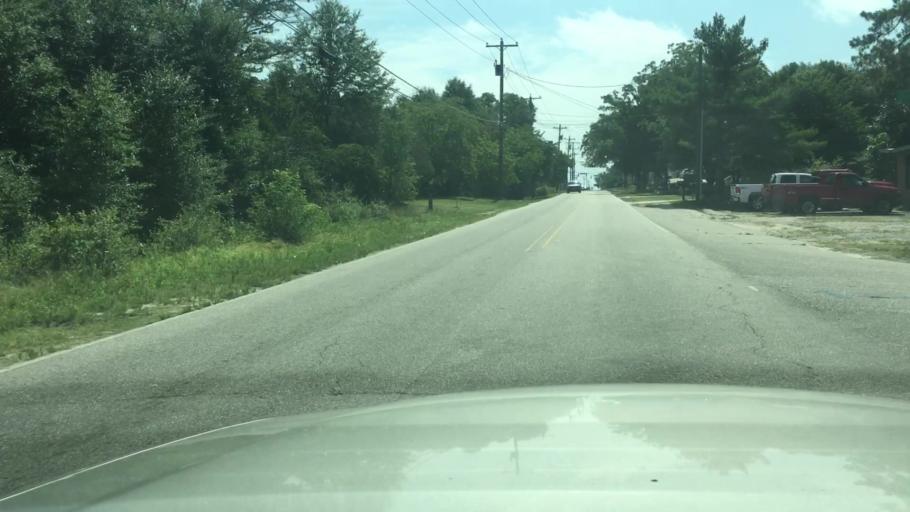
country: US
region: North Carolina
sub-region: Cumberland County
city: Fayetteville
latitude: 35.0137
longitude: -78.9009
